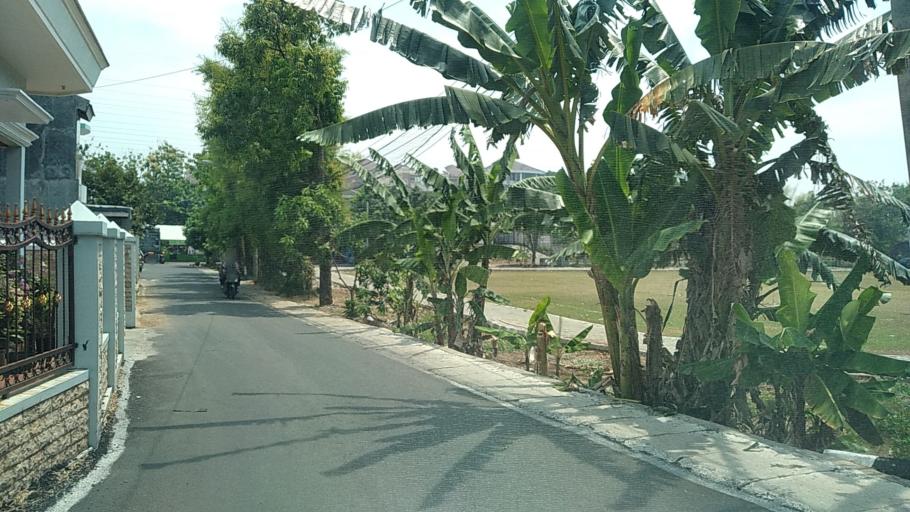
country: ID
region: Central Java
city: Semarang
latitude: -7.0515
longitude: 110.4284
